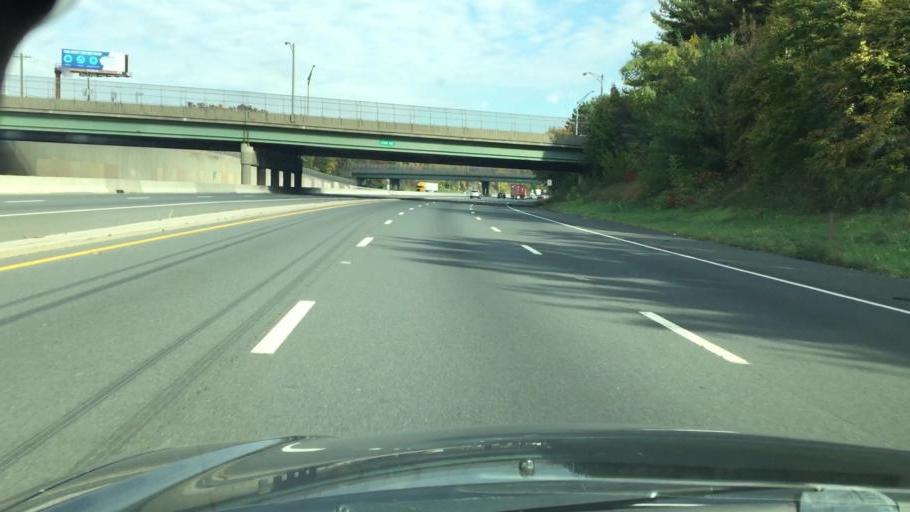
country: US
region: New Jersey
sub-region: Union County
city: Hillside
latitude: 40.7136
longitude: -74.2233
